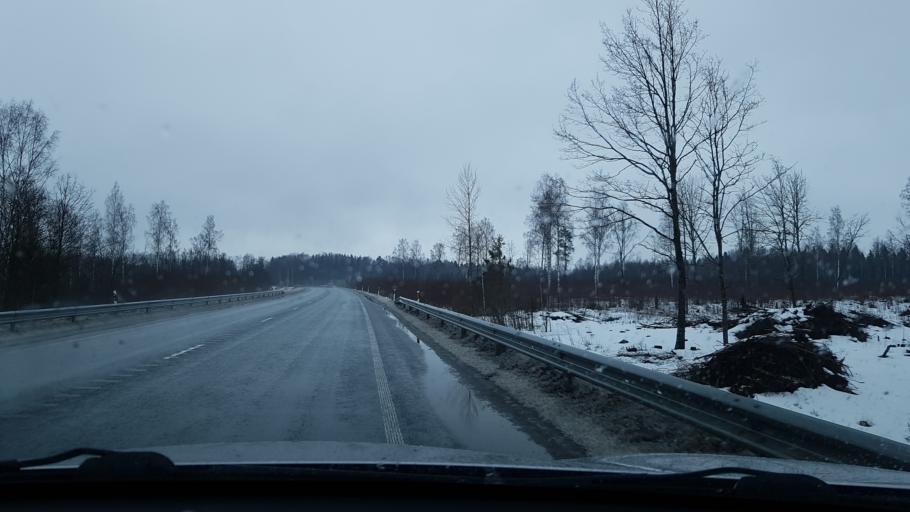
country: EE
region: Raplamaa
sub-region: Kohila vald
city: Kohila
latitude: 59.1345
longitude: 24.7922
